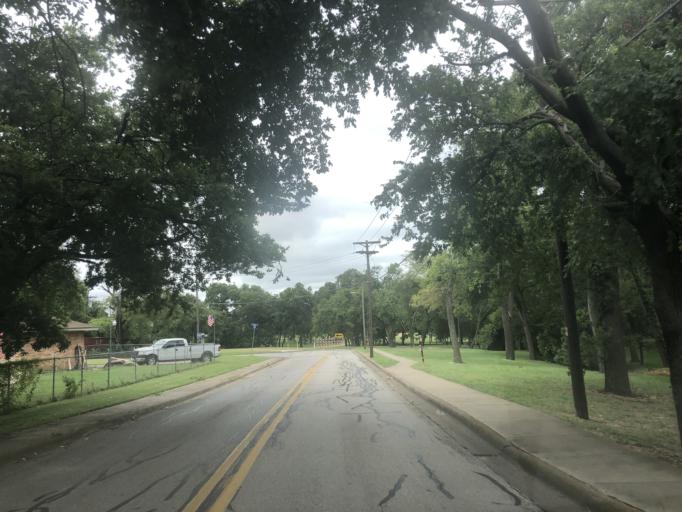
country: US
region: Texas
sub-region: Dallas County
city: Duncanville
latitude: 32.6560
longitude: -96.9174
